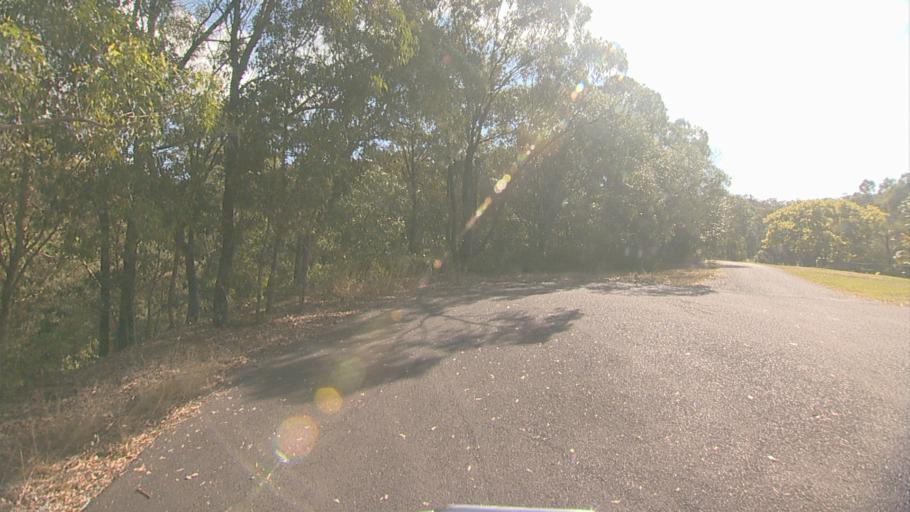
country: AU
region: Queensland
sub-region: Logan
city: Windaroo
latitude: -27.7330
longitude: 153.1881
